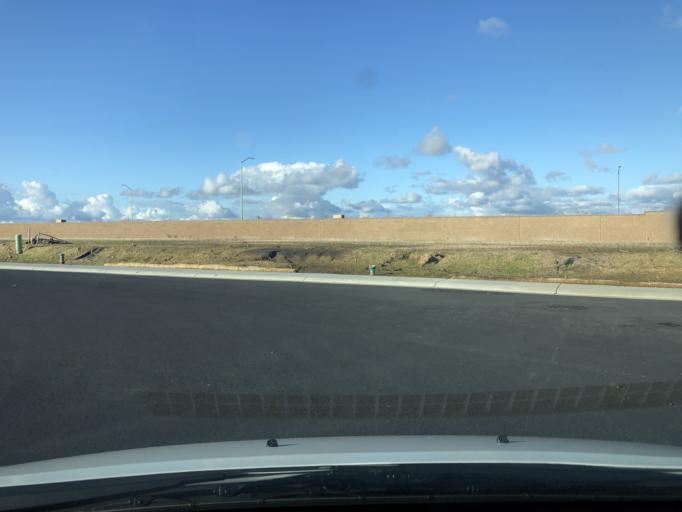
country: US
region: California
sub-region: Sacramento County
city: North Highlands
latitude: 38.7746
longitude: -121.3935
